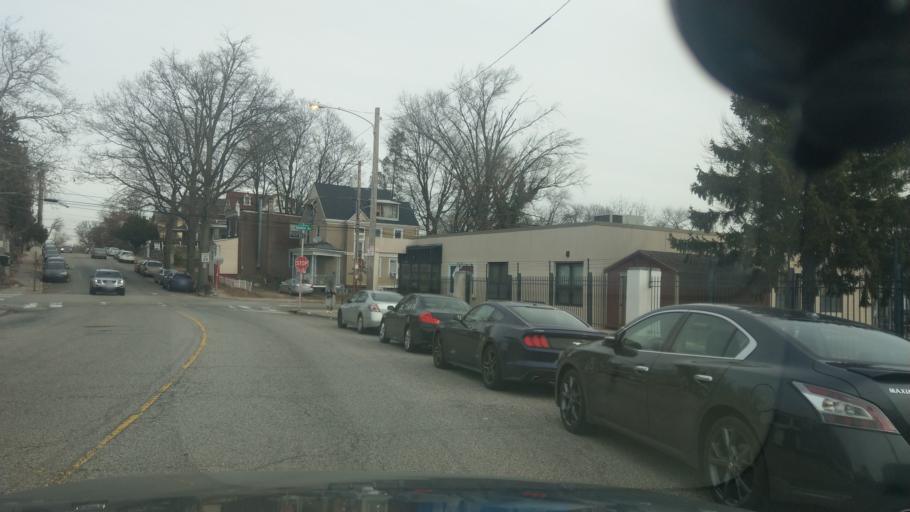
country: US
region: Pennsylvania
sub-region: Montgomery County
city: Wyncote
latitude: 40.0418
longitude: -75.1387
